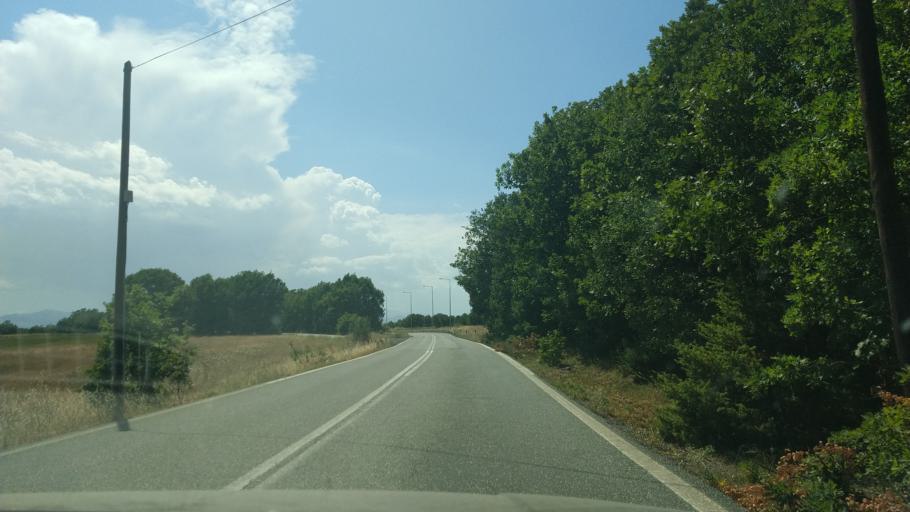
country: GR
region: West Macedonia
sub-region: Nomos Grevenon
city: Grevena
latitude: 40.0673
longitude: 21.4475
